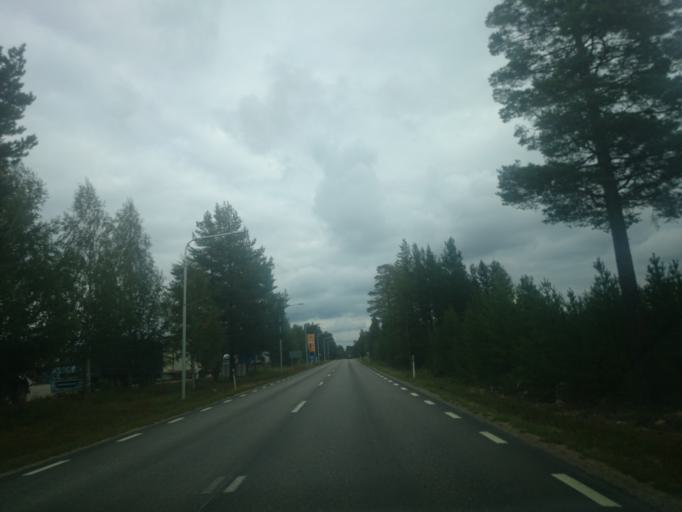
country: SE
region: Jaemtland
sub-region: Harjedalens Kommun
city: Sveg
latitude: 62.0364
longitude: 14.3852
